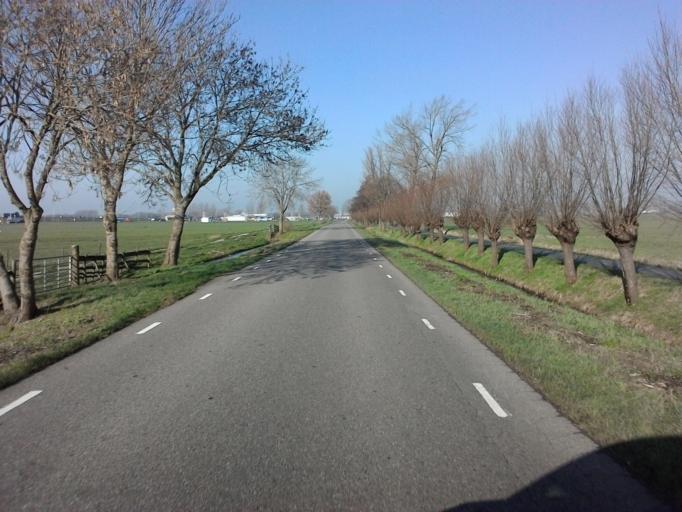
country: NL
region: South Holland
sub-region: Gemeente Gorinchem
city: Gorinchem
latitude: 51.8943
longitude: 4.9839
